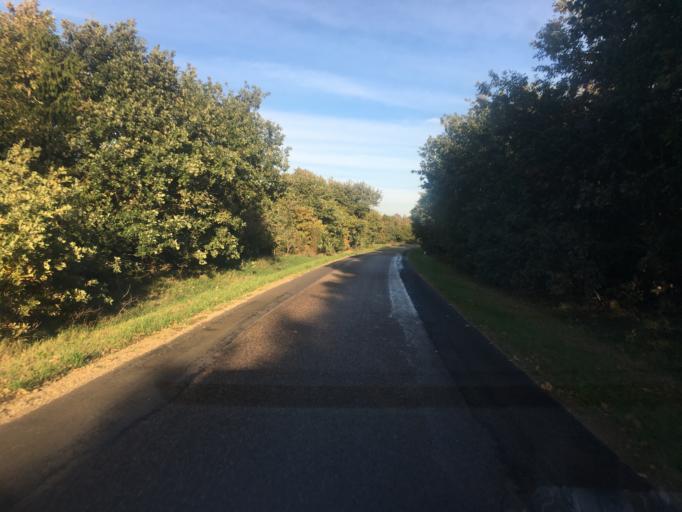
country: DE
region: Schleswig-Holstein
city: Ellhoft
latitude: 54.9158
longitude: 8.9465
